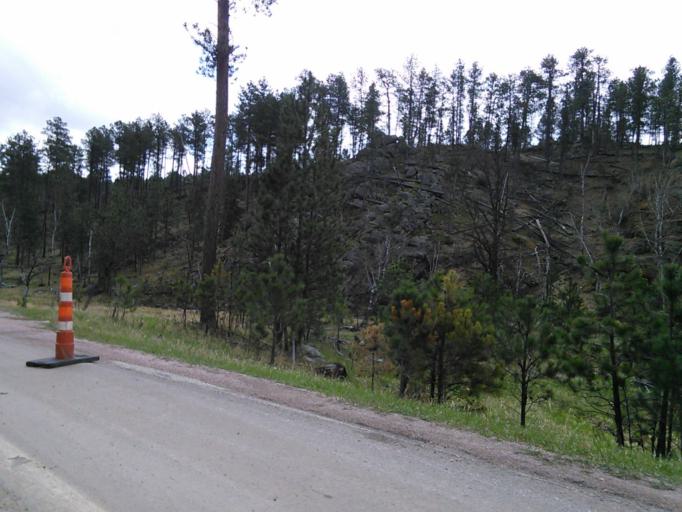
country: US
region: South Dakota
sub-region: Custer County
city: Custer
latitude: 43.7604
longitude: -103.4774
